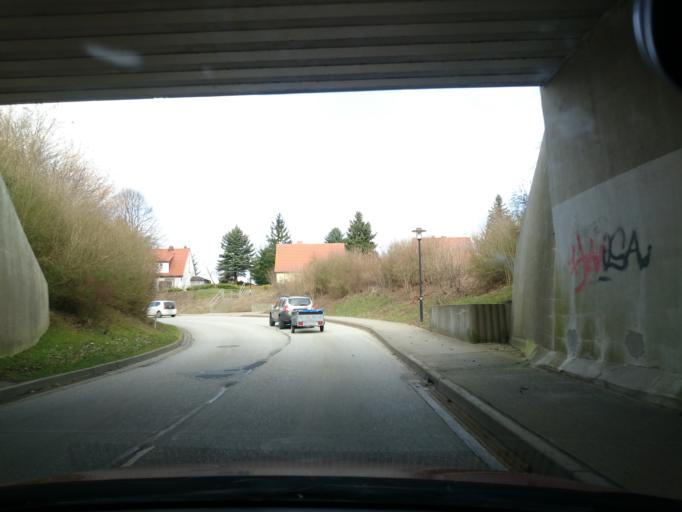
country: DE
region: Mecklenburg-Vorpommern
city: Velgast
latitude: 54.2780
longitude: 12.8072
